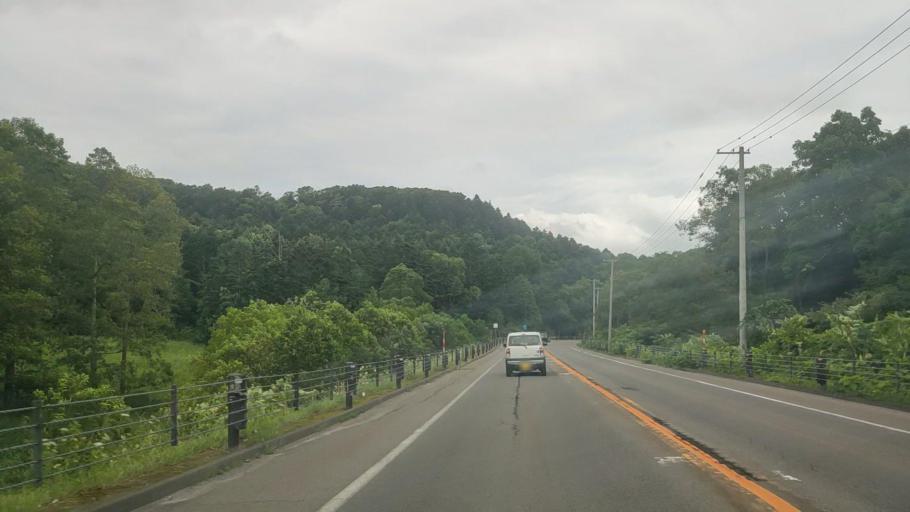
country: JP
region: Hokkaido
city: Nanae
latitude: 41.9664
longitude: 140.6500
